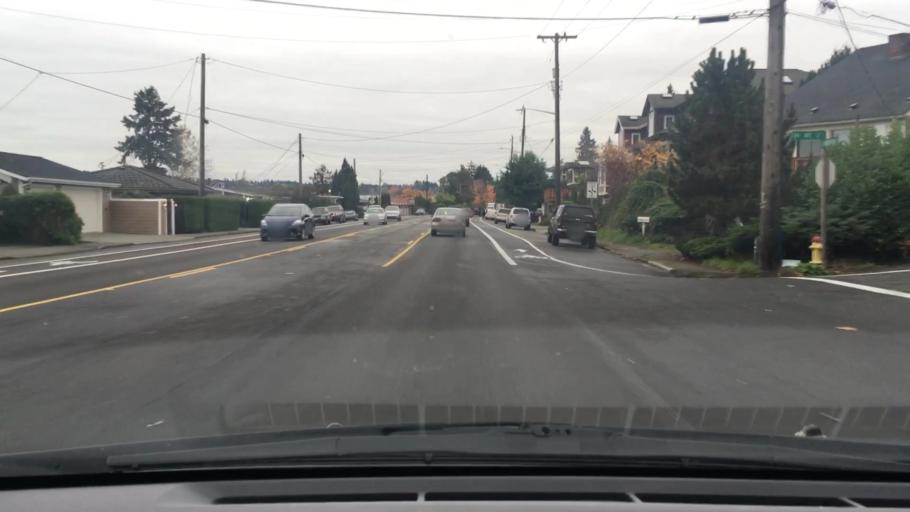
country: US
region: Washington
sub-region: King County
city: Bryn Mawr-Skyway
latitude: 47.5044
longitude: -122.2275
